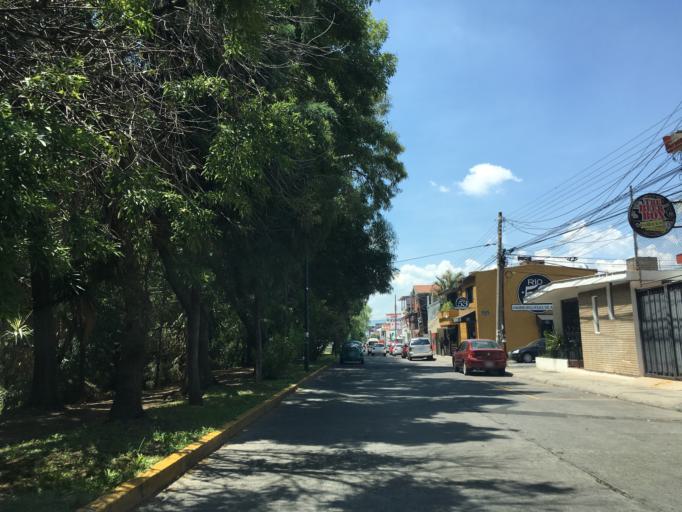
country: MX
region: Michoacan
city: Morelia
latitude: 19.6853
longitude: -101.1690
